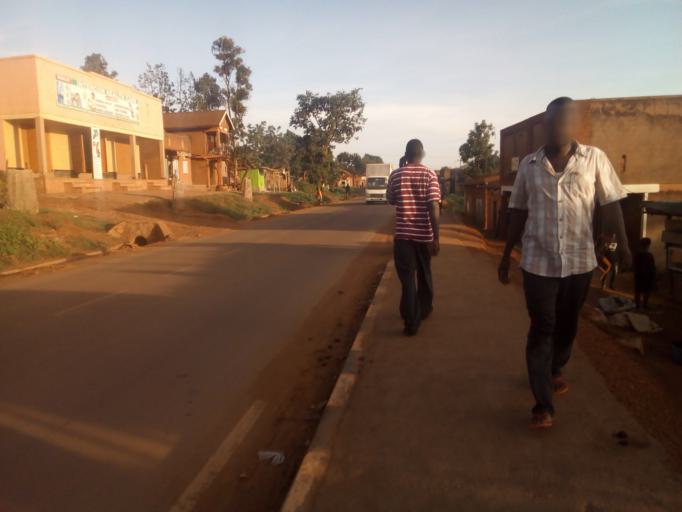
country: UG
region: Central Region
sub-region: Wakiso District
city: Kajansi
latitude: 0.2480
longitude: 32.5711
